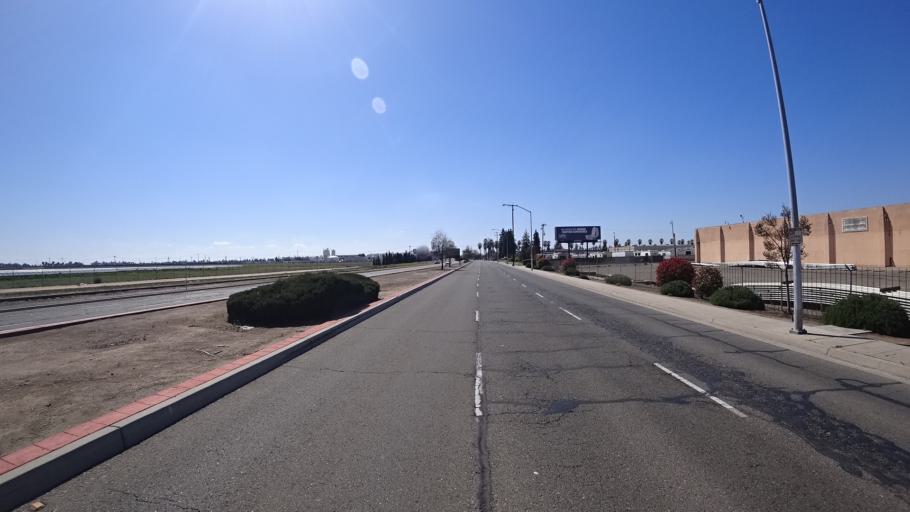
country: US
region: California
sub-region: Fresno County
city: Sunnyside
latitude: 36.7638
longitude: -119.7004
